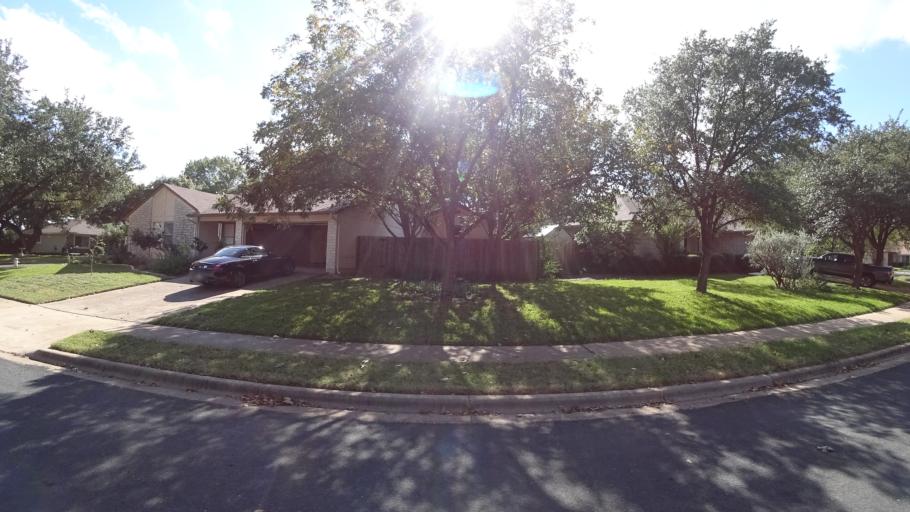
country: US
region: Texas
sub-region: Travis County
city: Wells Branch
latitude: 30.4257
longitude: -97.7264
